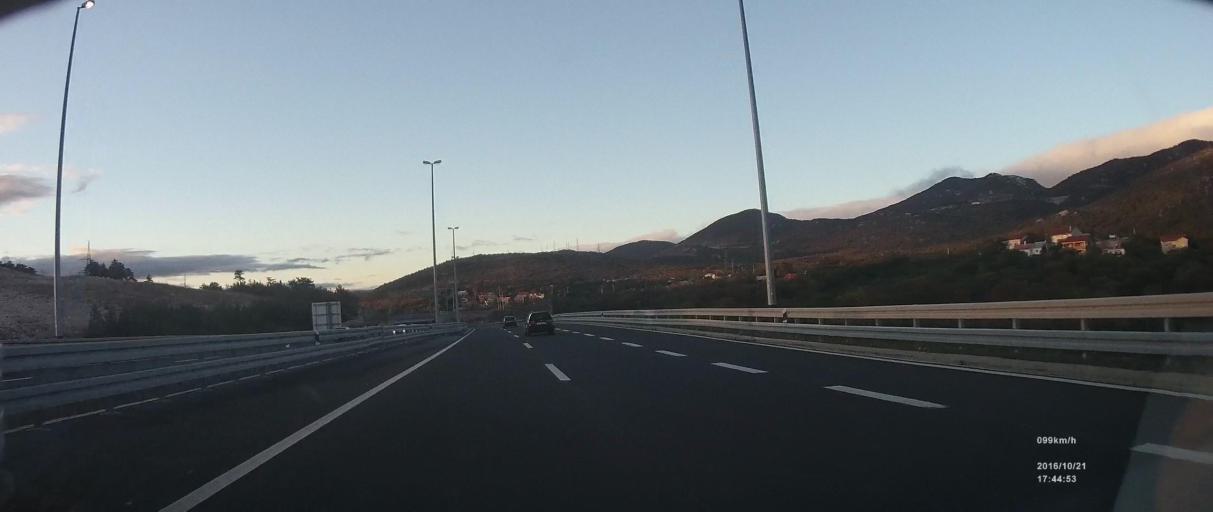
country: HR
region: Primorsko-Goranska
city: Hreljin
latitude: 45.2855
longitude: 14.5878
